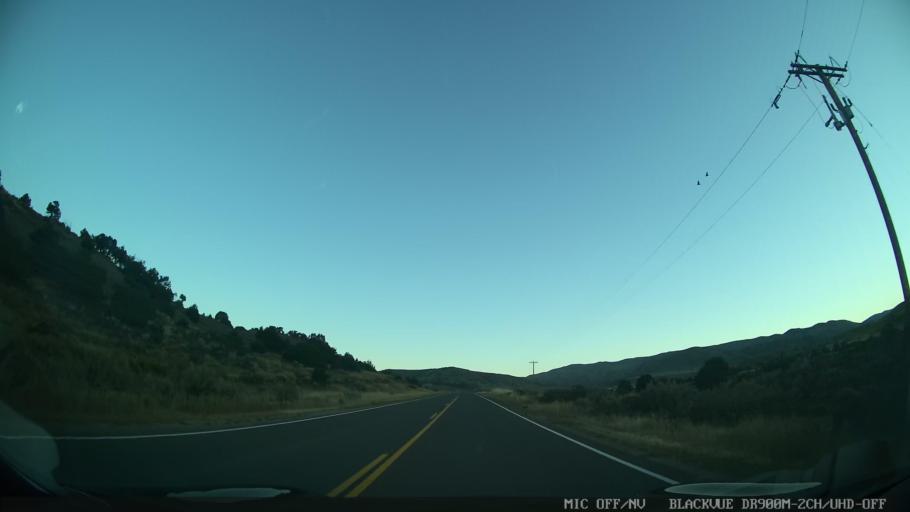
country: US
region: Colorado
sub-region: Eagle County
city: Edwards
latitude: 39.7300
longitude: -106.6785
